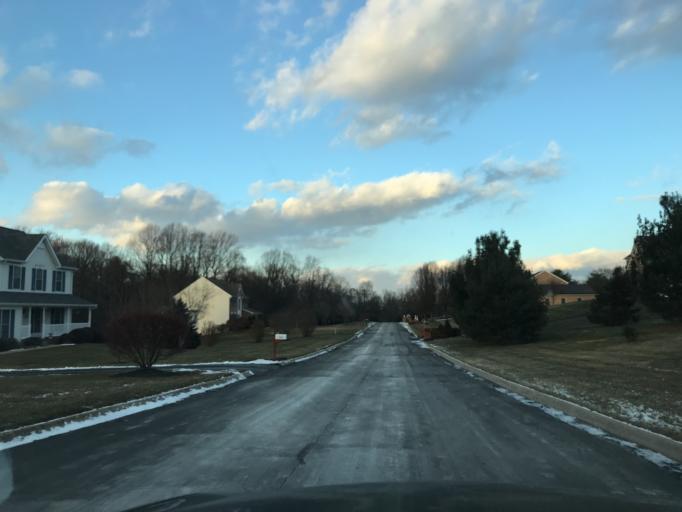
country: US
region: Maryland
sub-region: Harford County
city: Bel Air North
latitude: 39.5895
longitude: -76.3704
